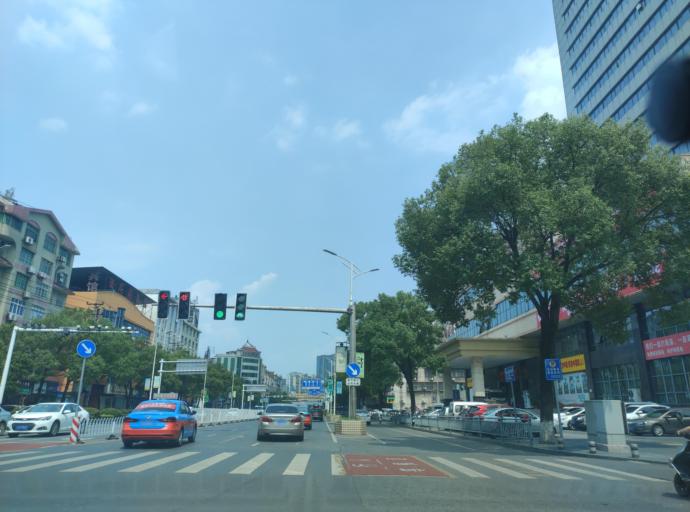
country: CN
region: Jiangxi Sheng
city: Pingxiang
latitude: 27.6431
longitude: 113.8628
